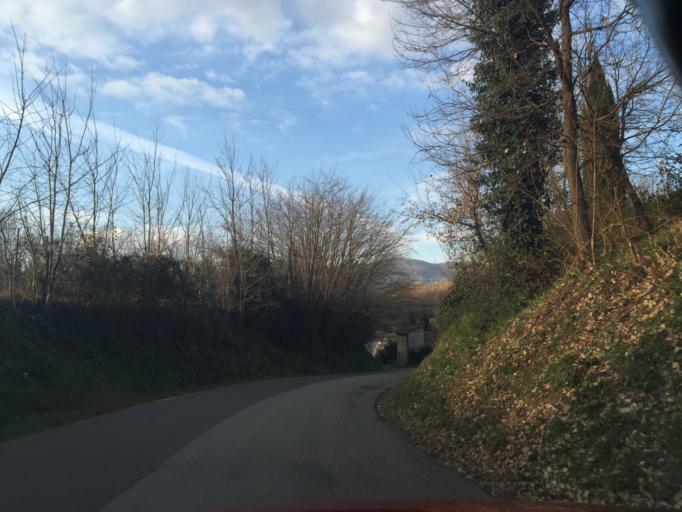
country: IT
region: Tuscany
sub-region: Provincia di Pistoia
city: San Rocco
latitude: 43.8393
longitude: 10.8672
